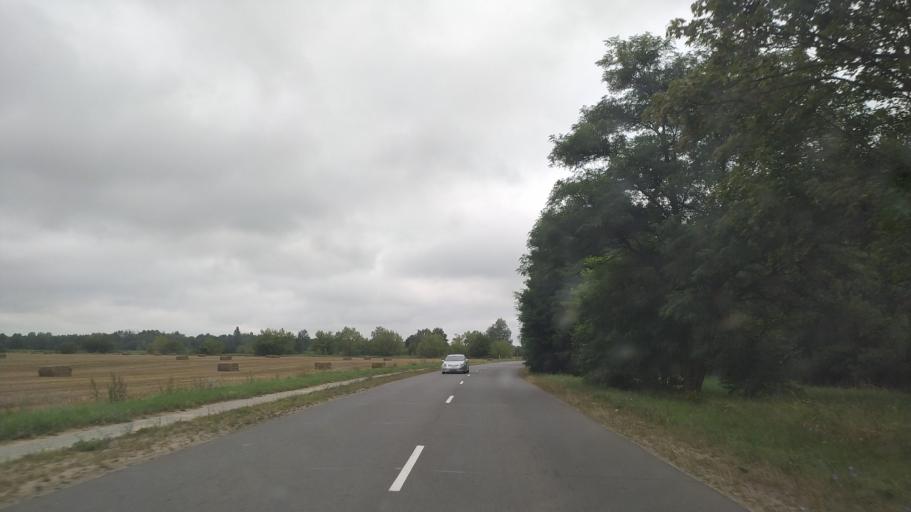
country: BY
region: Brest
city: Byaroza
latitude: 52.5562
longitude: 24.9185
